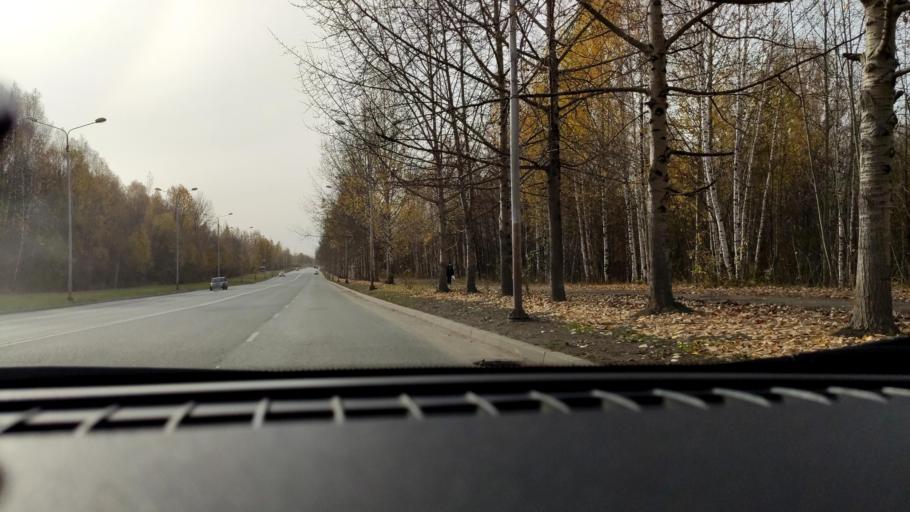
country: RU
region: Perm
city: Perm
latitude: 58.1064
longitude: 56.3948
